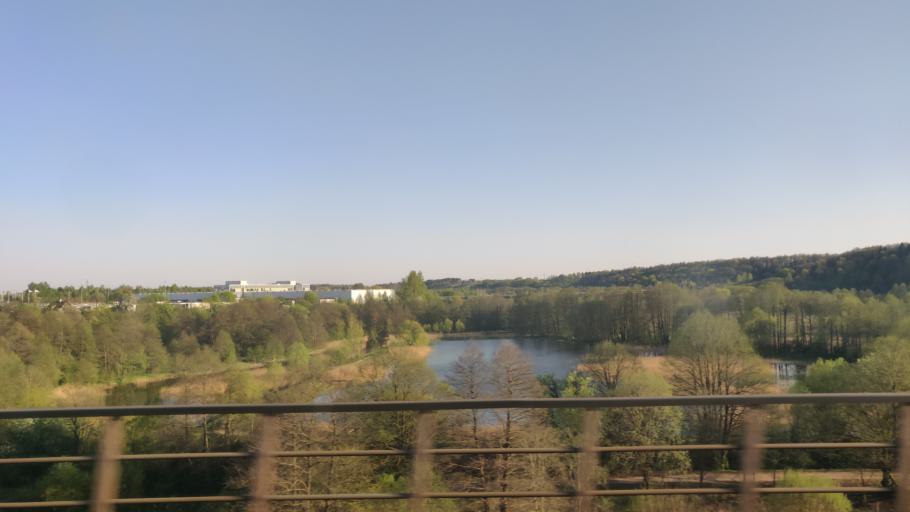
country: LT
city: Grigiskes
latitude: 54.6334
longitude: 25.1229
